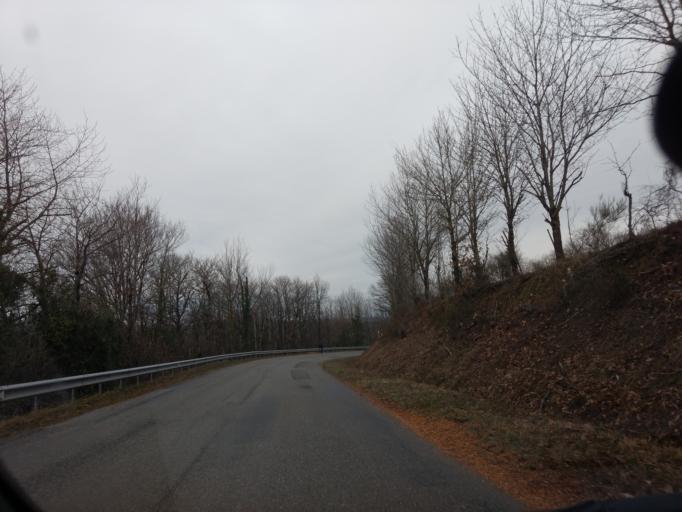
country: FR
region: Midi-Pyrenees
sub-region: Departement de l'Aveyron
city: Saint-Christophe-Vallon
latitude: 44.4308
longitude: 2.3422
